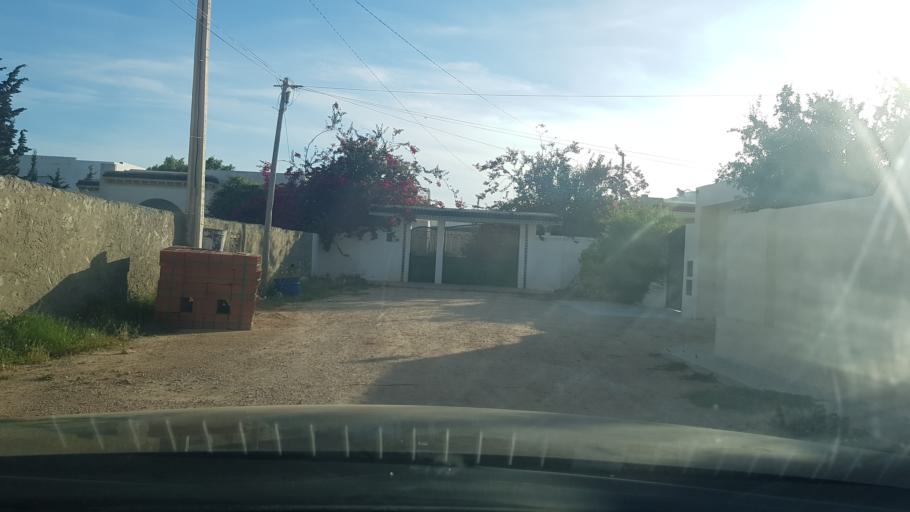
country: TN
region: Safaqis
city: Al Qarmadah
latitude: 34.8308
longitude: 10.7611
